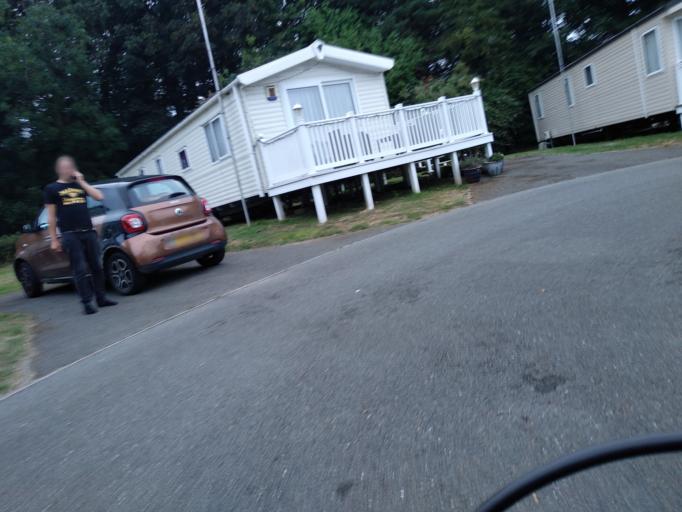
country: GB
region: England
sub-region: Isle of Wight
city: Shanklin
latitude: 50.6339
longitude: -1.1876
